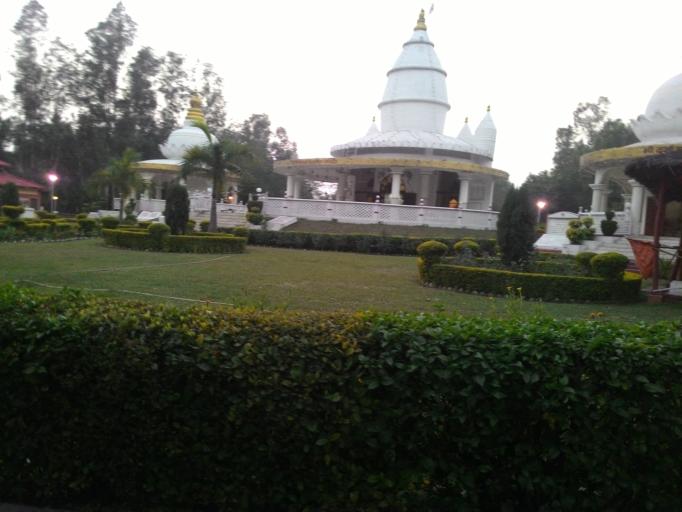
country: IN
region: Jharkhand
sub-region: Garhwa
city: Garwa
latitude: 24.2292
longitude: 83.8830
